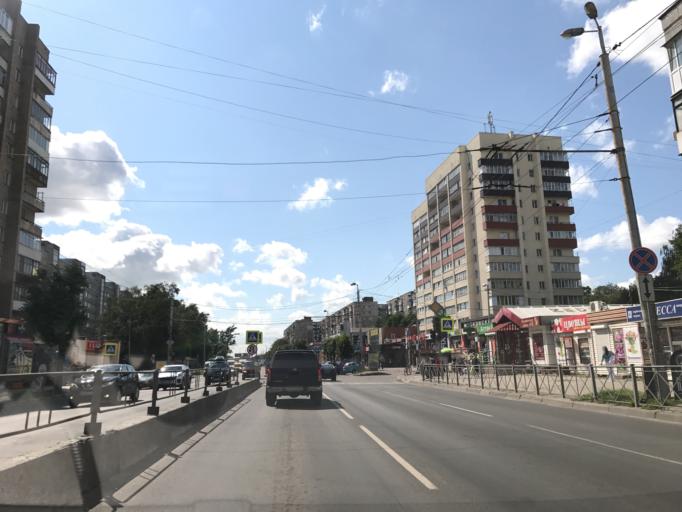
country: RU
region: Kaliningrad
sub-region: Gorod Kaliningrad
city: Kaliningrad
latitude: 54.7099
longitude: 20.5330
